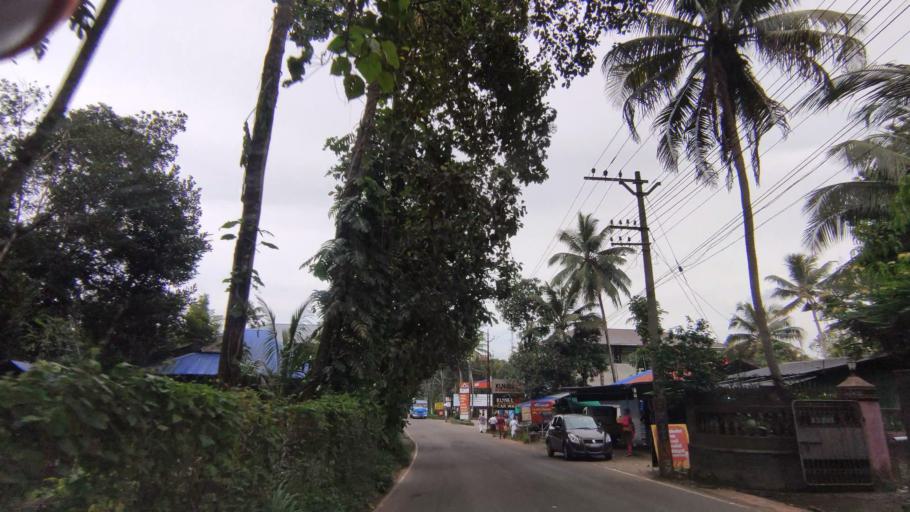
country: IN
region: Kerala
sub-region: Kottayam
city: Kottayam
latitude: 9.6642
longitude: 76.5317
